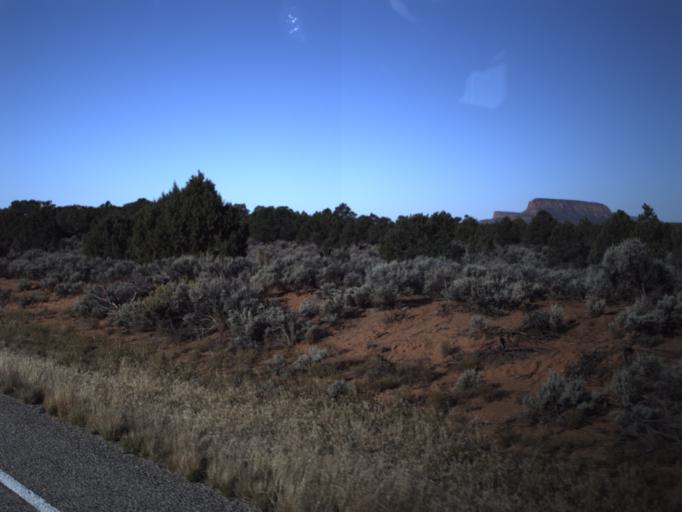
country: US
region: Utah
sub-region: San Juan County
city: Blanding
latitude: 37.5502
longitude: -109.9402
